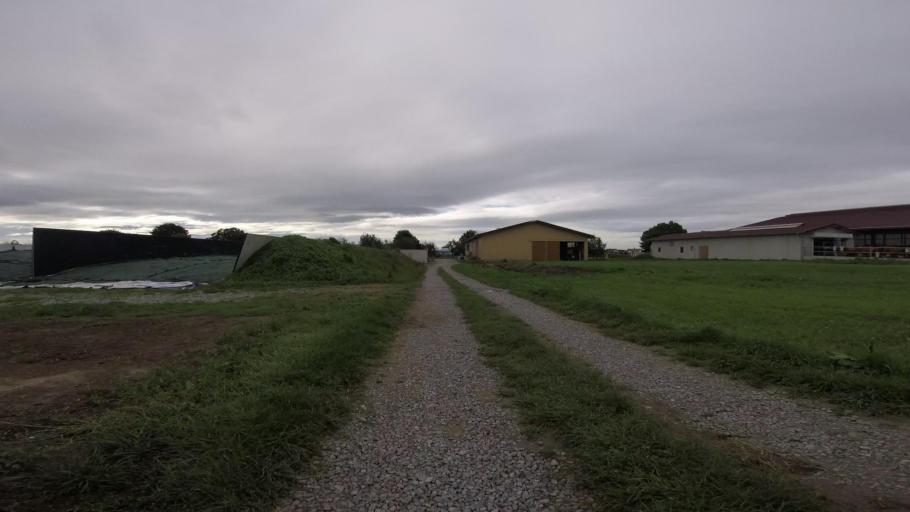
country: DE
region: Baden-Wuerttemberg
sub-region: Regierungsbezirk Stuttgart
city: Aspach
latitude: 48.9681
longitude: 9.4095
